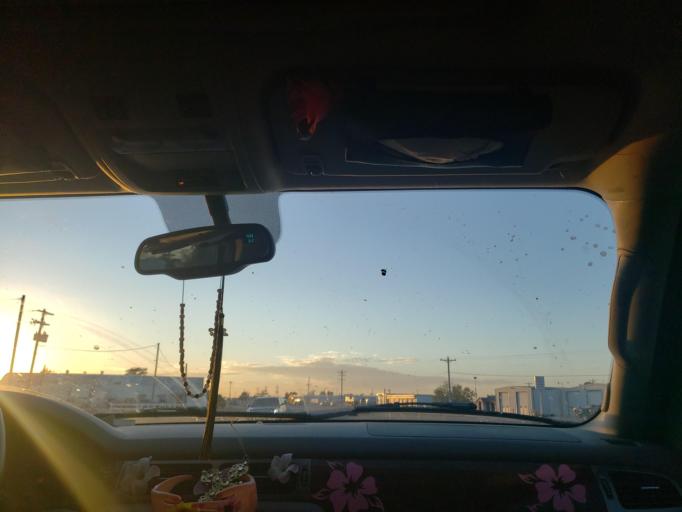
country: US
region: Kansas
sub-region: Finney County
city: Garden City
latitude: 37.9892
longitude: -100.9170
